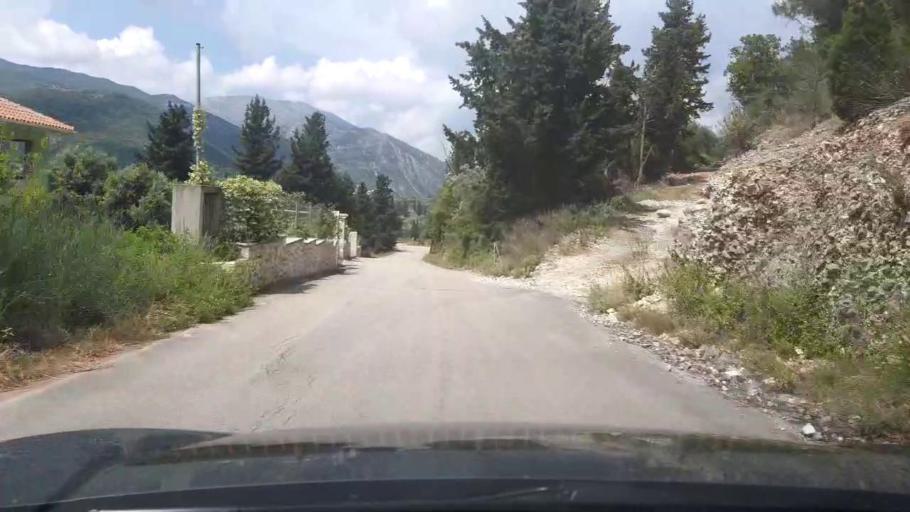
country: GR
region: Ionian Islands
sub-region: Lefkada
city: Nidri
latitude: 38.6475
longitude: 20.7044
